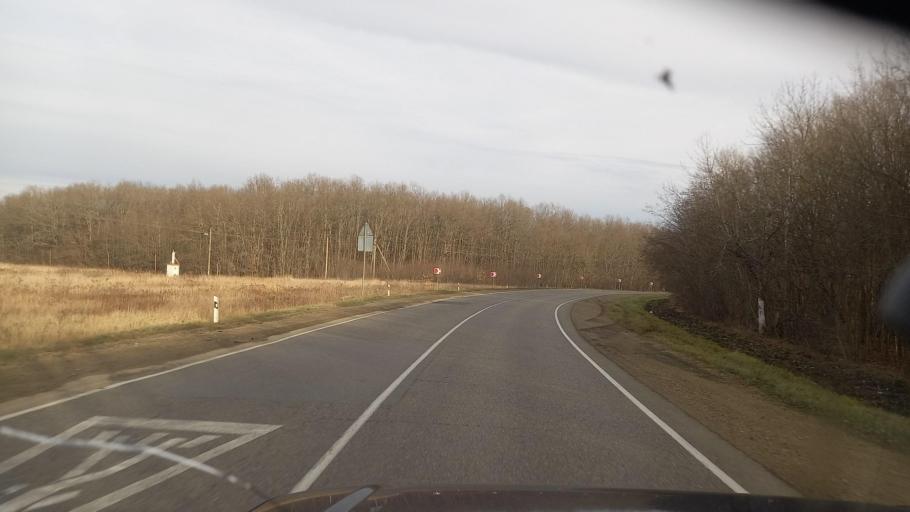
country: RU
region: Krasnodarskiy
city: Khadyzhensk
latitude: 44.6373
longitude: 39.5109
